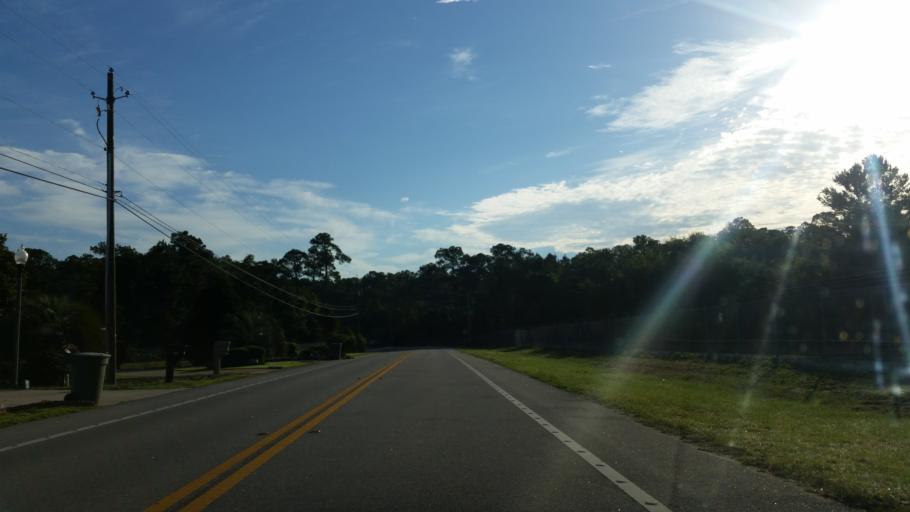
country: US
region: Florida
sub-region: Escambia County
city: Warrington
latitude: 30.3425
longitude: -87.3437
